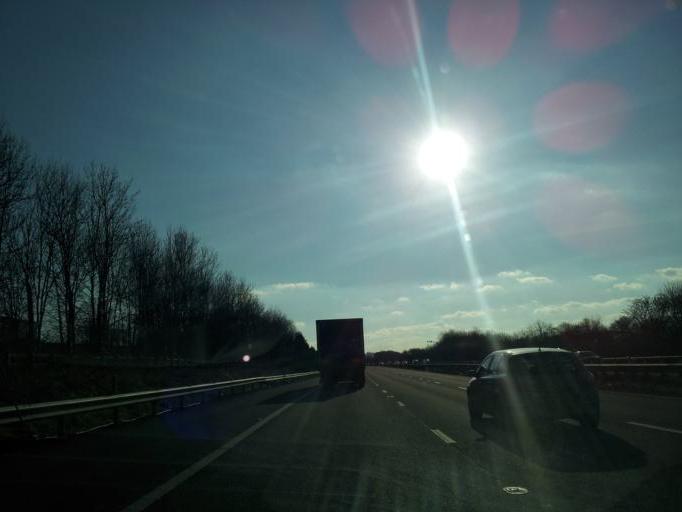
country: GB
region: England
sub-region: Devon
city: Bradninch
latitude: 50.8163
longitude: -3.4148
